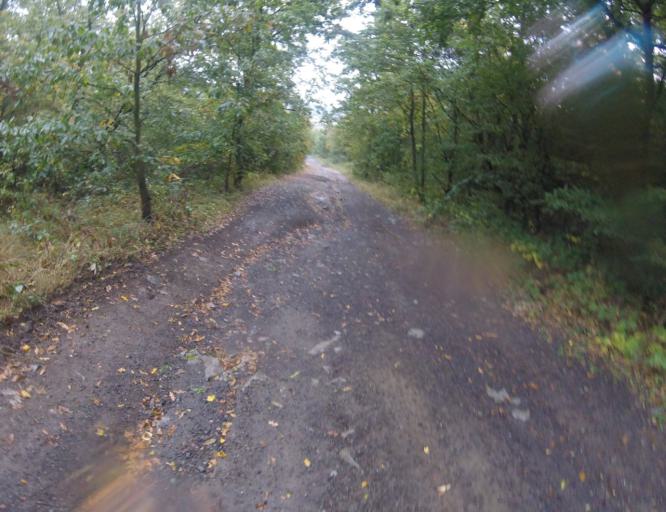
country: HU
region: Pest
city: Szob
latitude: 47.8556
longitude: 18.8772
